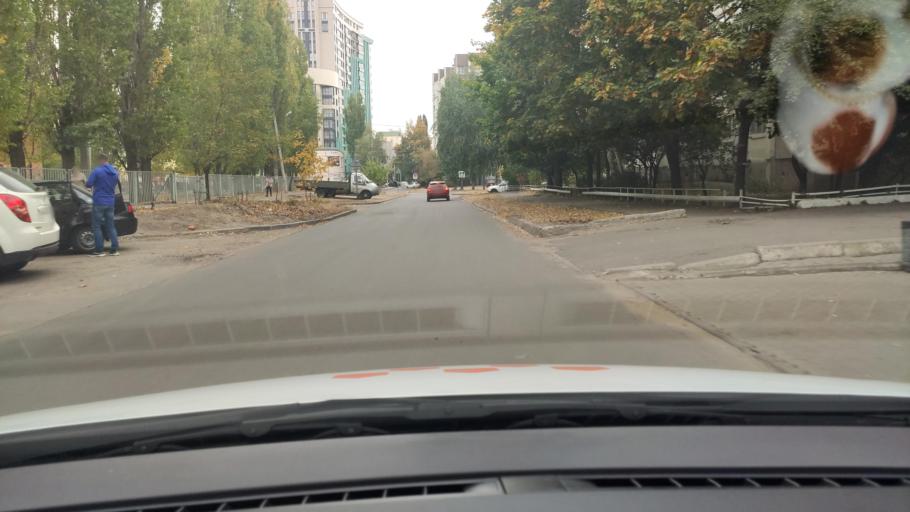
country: RU
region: Voronezj
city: Podgornoye
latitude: 51.7157
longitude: 39.1673
